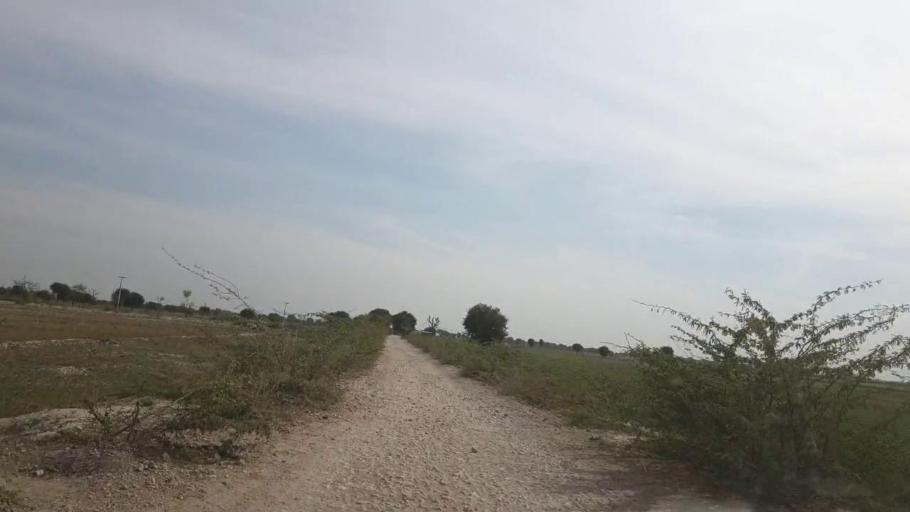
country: PK
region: Sindh
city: Nabisar
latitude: 25.0408
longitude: 69.5616
